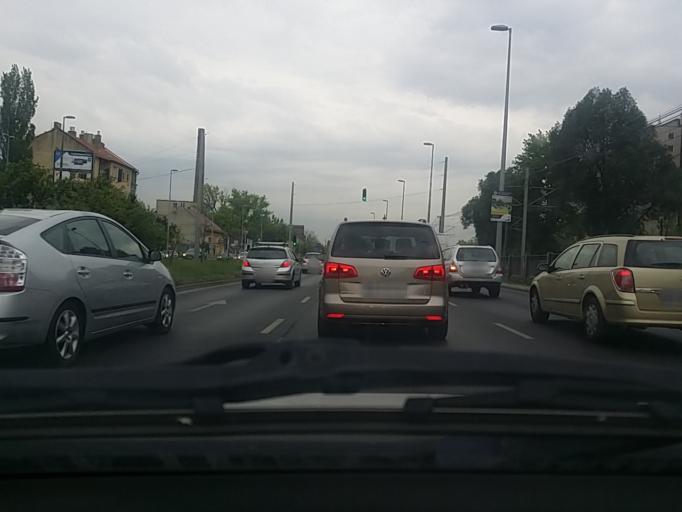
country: HU
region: Budapest
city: Budapest III. keruelet
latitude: 47.5589
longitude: 19.0465
